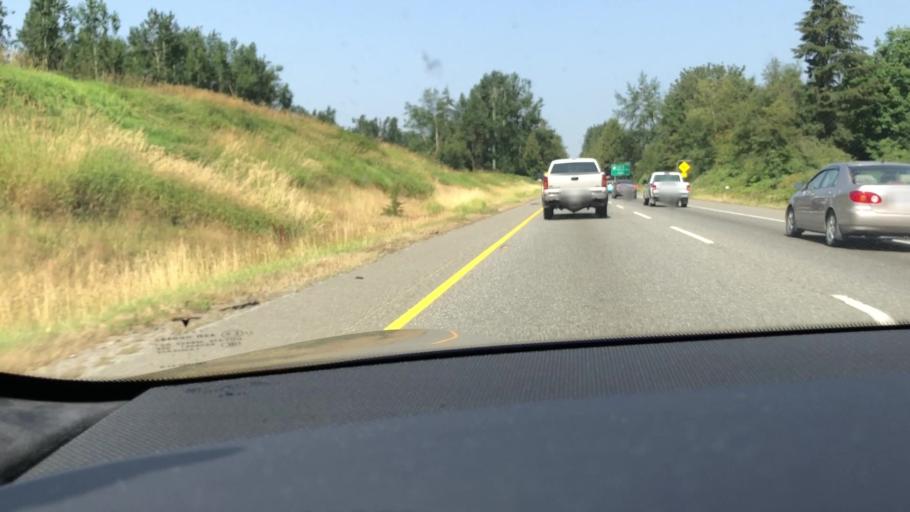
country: CA
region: British Columbia
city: Aldergrove
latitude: 49.0934
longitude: -122.4714
